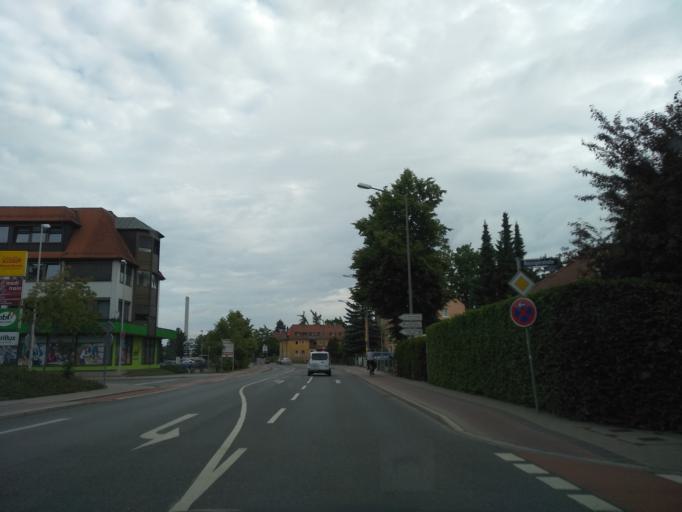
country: DE
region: Bavaria
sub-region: Regierungsbezirk Mittelfranken
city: Erlangen
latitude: 49.5821
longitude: 11.0059
